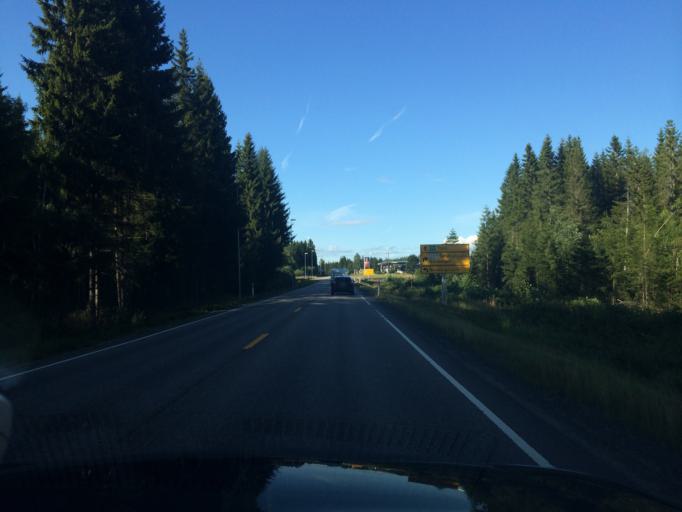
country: NO
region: Hedmark
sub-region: Elverum
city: Elverum
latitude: 60.9302
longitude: 11.6724
